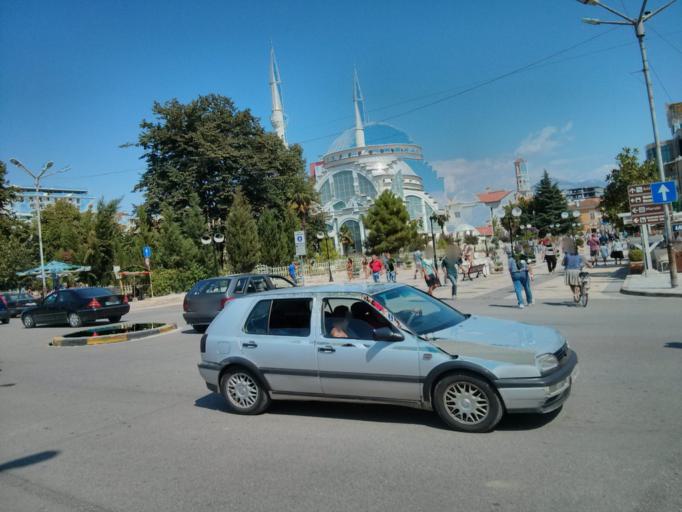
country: AL
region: Shkoder
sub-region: Rrethi i Shkodres
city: Shkoder
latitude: 42.0660
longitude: 19.5131
